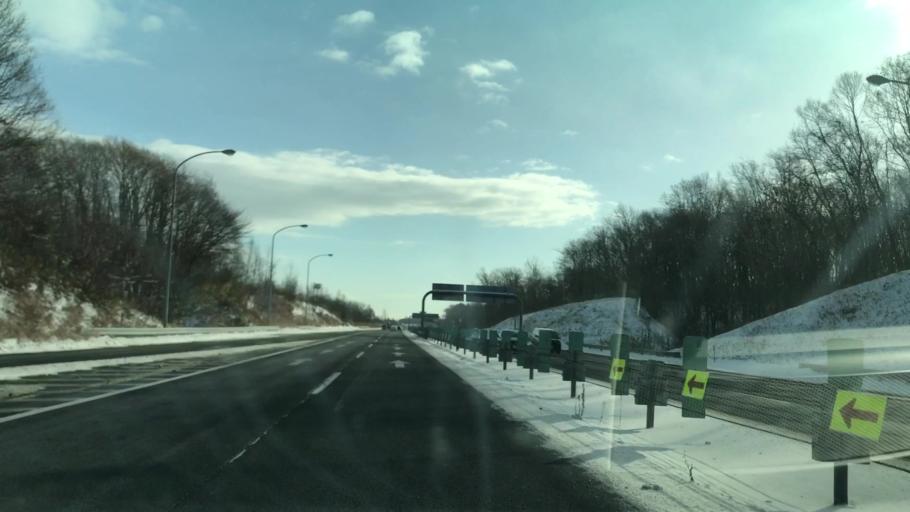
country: JP
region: Hokkaido
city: Chitose
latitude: 42.8439
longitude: 141.5895
